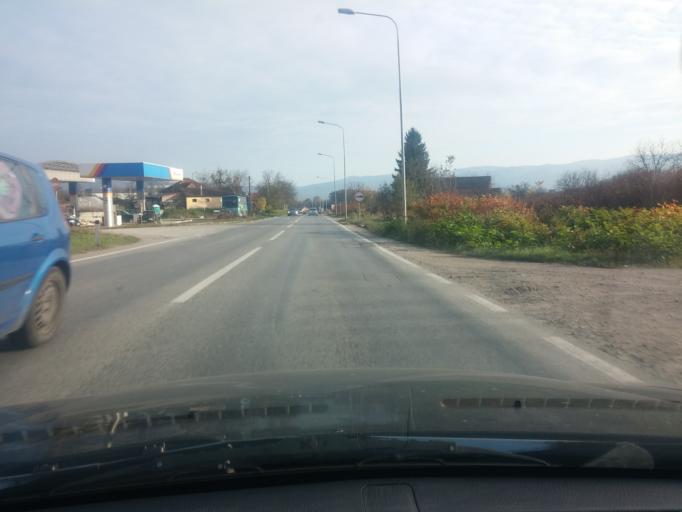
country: BA
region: Republika Srpska
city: Banja Luka
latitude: 44.8260
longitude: 17.1911
